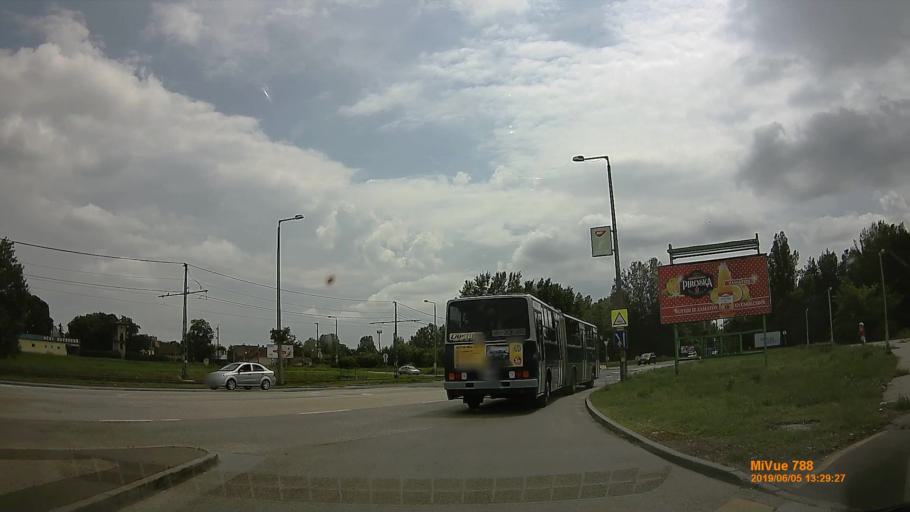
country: HU
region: Budapest
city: Budapest XV. keruelet
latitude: 47.5776
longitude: 19.1152
